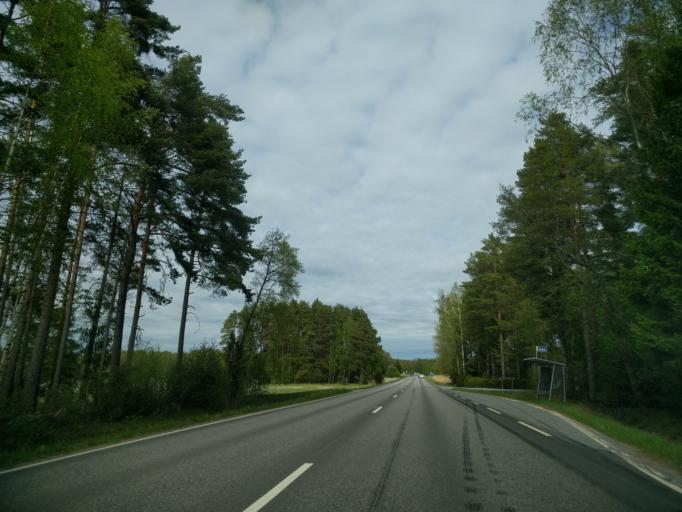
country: FI
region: Varsinais-Suomi
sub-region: Vakka-Suomi
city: Taivassalo
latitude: 60.5669
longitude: 21.6255
